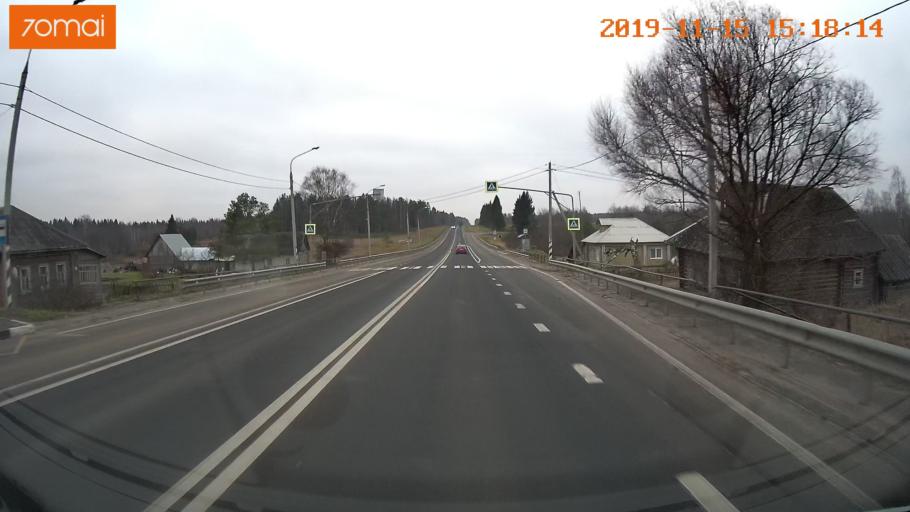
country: RU
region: Jaroslavl
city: Danilov
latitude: 58.2502
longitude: 40.1807
